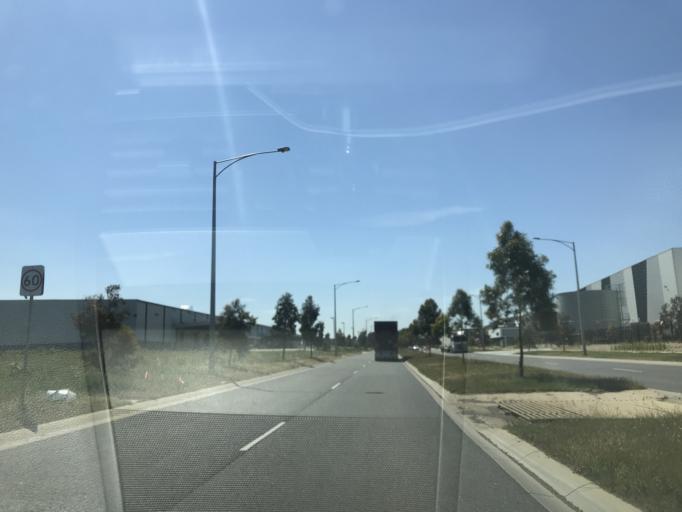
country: AU
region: Victoria
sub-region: Wyndham
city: Truganina
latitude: -37.8224
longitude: 144.7644
